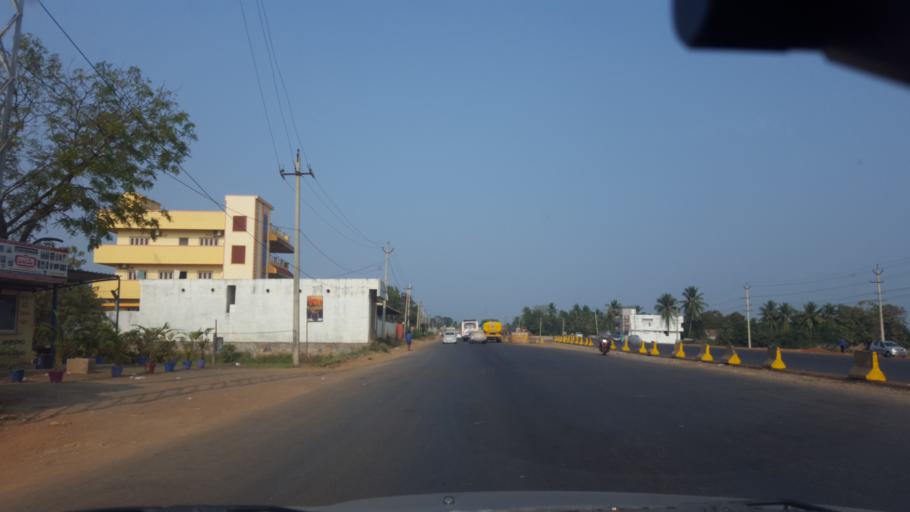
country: IN
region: Andhra Pradesh
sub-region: West Godavari
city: Eluru
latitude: 16.6660
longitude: 81.0093
